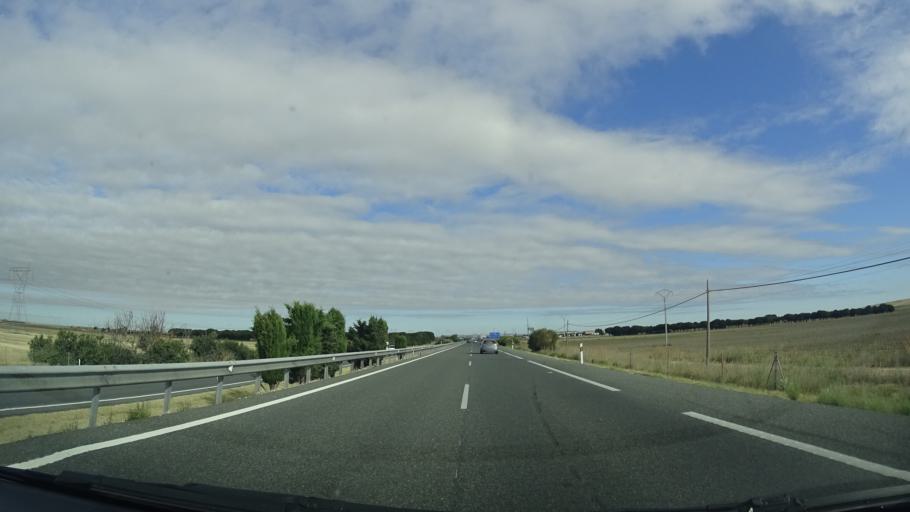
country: ES
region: Castille and Leon
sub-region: Provincia de Valladolid
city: San Vicente del Palacio
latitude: 41.2138
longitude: -4.8358
